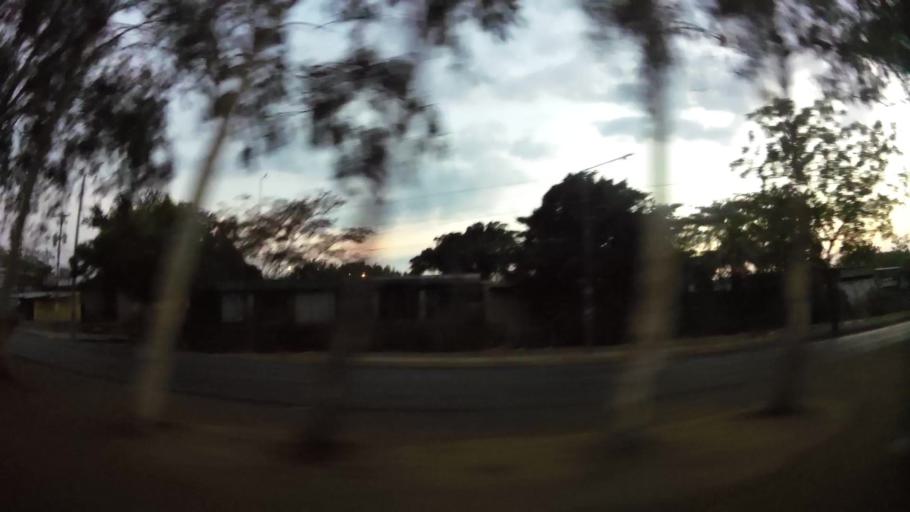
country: NI
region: Managua
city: Managua
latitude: 12.1267
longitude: -86.2419
